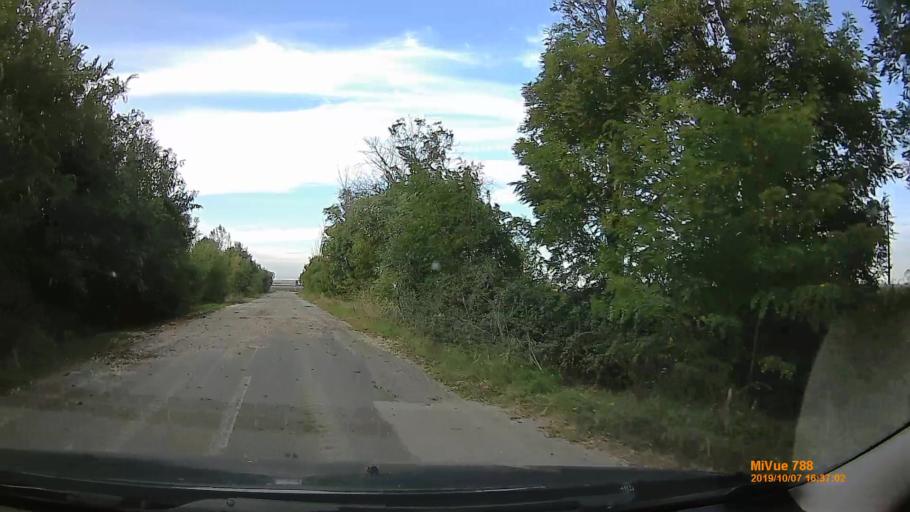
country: HU
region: Bekes
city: Szarvas
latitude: 46.8161
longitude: 20.6066
